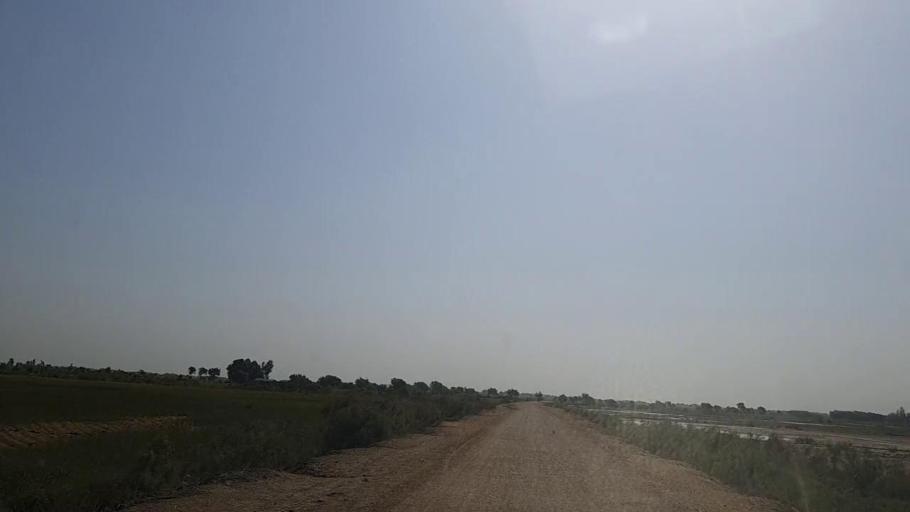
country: PK
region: Sindh
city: Daro Mehar
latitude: 24.7094
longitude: 68.1241
